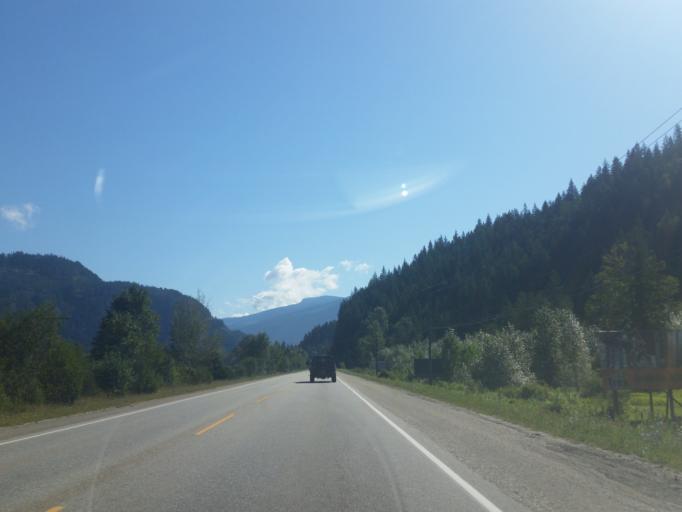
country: CA
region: British Columbia
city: Sicamous
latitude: 50.8856
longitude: -118.8985
